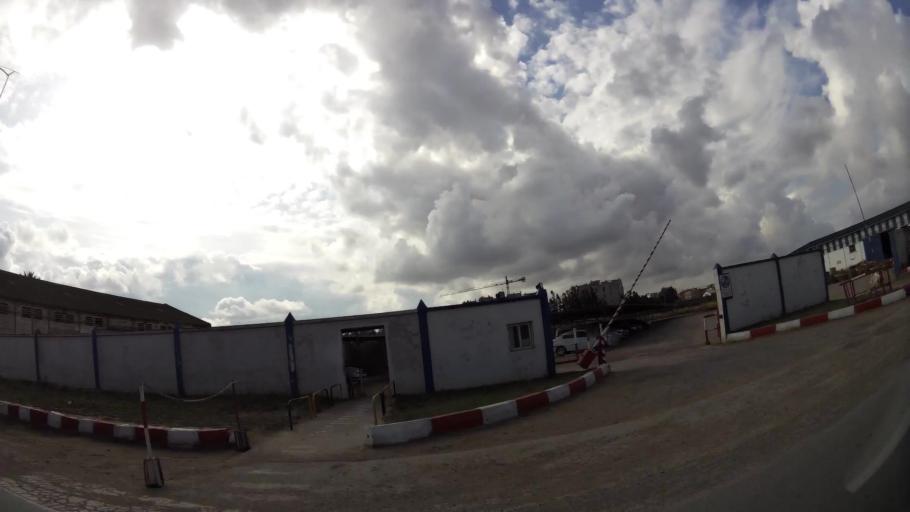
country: MA
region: Gharb-Chrarda-Beni Hssen
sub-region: Kenitra Province
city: Kenitra
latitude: 34.2754
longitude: -6.5612
